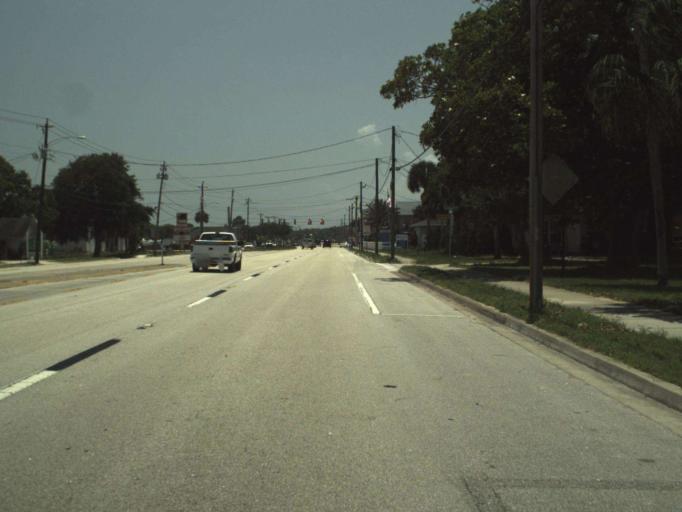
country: US
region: Florida
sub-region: Volusia County
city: Port Orange
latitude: 29.1271
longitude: -80.9795
